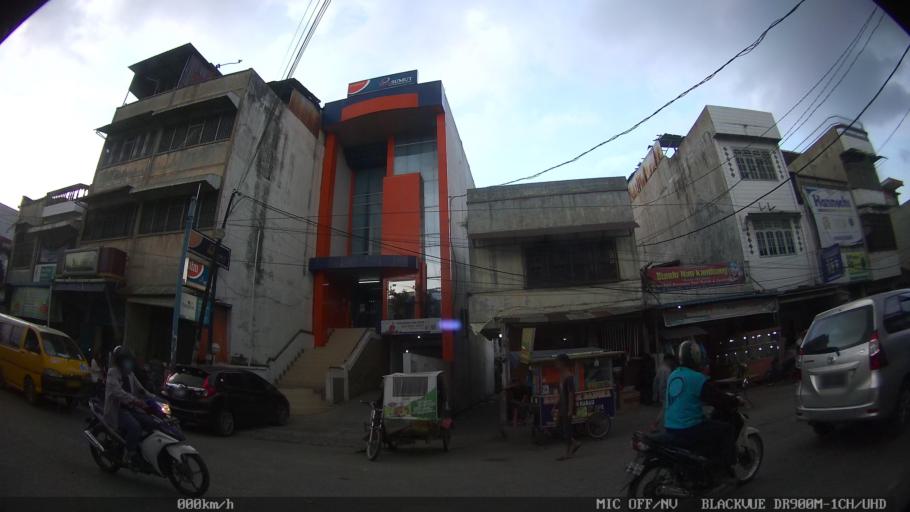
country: ID
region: North Sumatra
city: Medan
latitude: 3.5821
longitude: 98.7044
